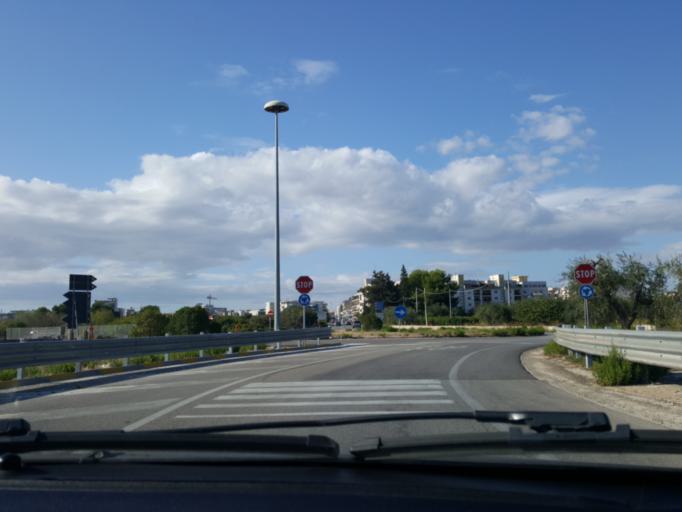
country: IT
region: Apulia
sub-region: Provincia di Bari
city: Triggiano
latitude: 41.0740
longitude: 16.9377
